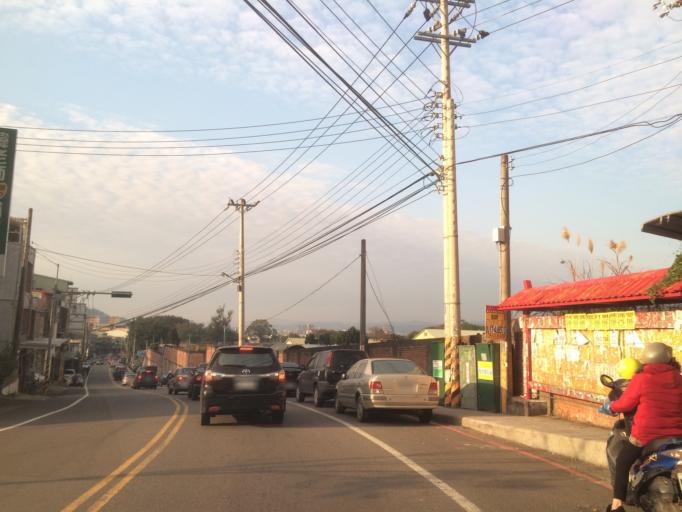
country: TW
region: Taiwan
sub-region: Hsinchu
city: Zhubei
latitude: 24.7155
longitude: 121.0981
